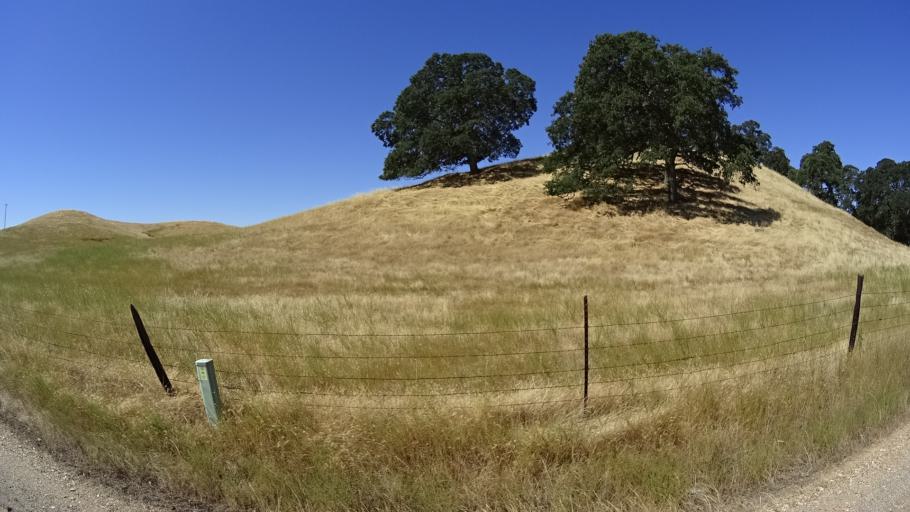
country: US
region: California
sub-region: Calaveras County
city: Rancho Calaveras
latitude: 38.0231
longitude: -120.8386
